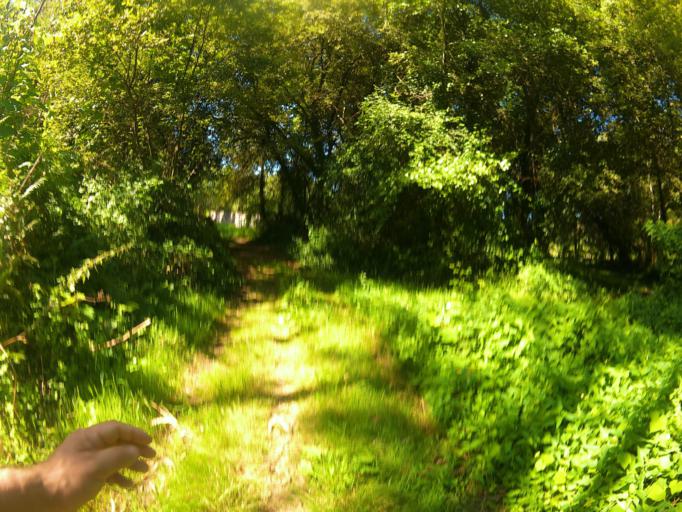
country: PT
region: Viana do Castelo
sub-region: Viana do Castelo
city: Darque
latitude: 41.7192
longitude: -8.6797
